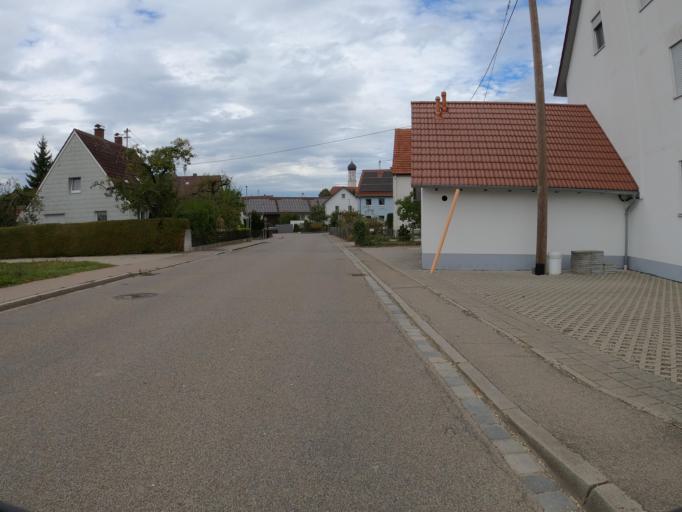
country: DE
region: Bavaria
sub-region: Swabia
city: Holzheim
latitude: 48.3801
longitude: 10.0766
